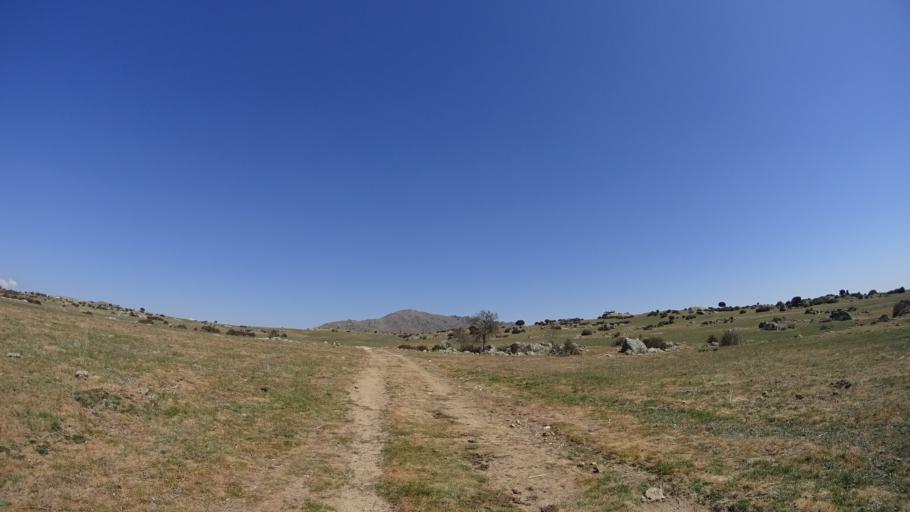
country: ES
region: Madrid
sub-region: Provincia de Madrid
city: Colmenar Viejo
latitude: 40.7052
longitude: -3.7551
